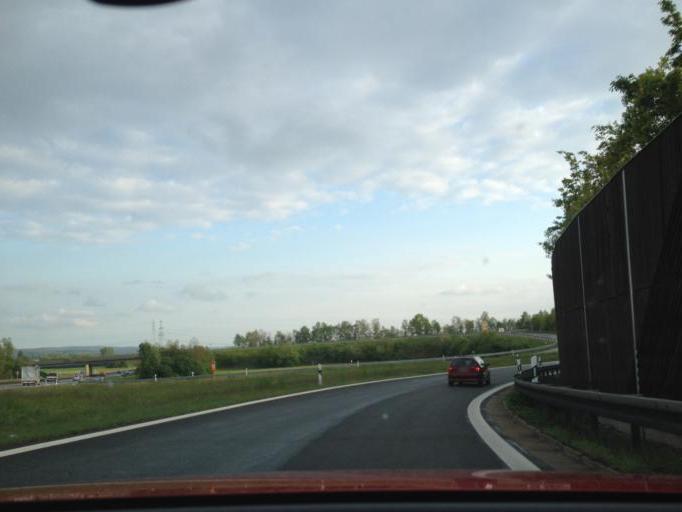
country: DE
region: Bavaria
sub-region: Upper Palatinate
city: Schirmitz
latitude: 49.6524
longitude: 12.1473
